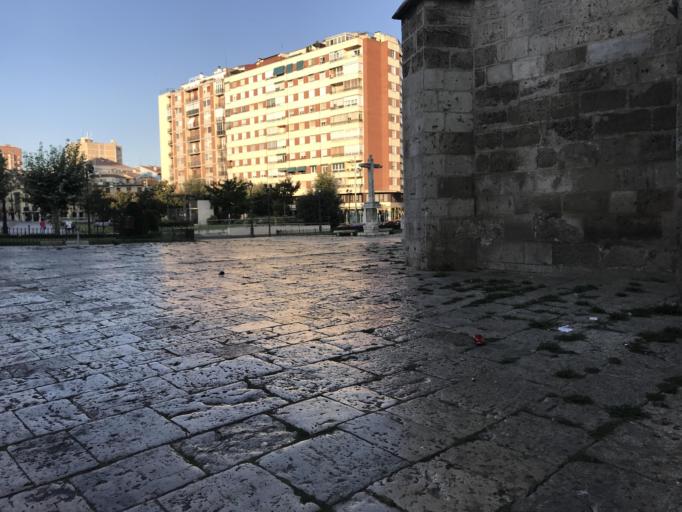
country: ES
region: Castille and Leon
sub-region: Provincia de Valladolid
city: Valladolid
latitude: 41.6539
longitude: -4.7227
